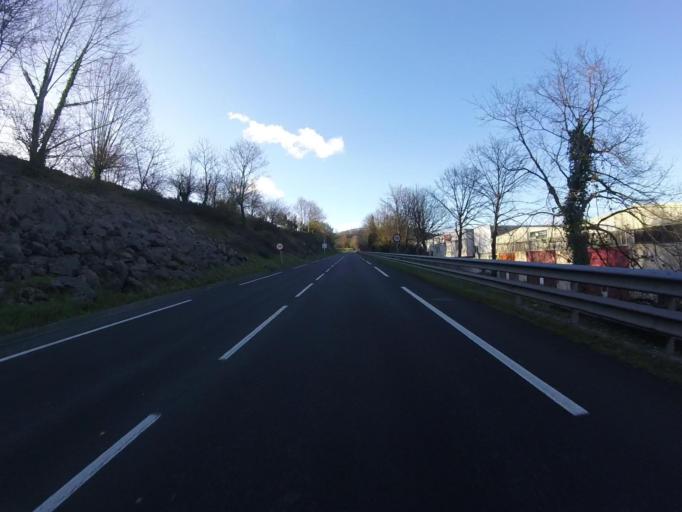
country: ES
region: Basque Country
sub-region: Provincia de Guipuzcoa
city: Errenteria
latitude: 43.2988
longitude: -1.8811
